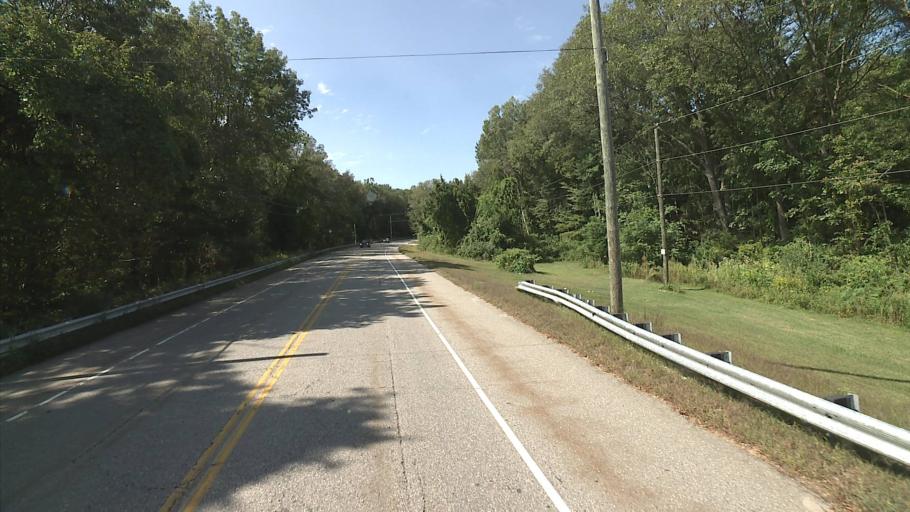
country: US
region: Connecticut
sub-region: New London County
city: Baltic
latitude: 41.5834
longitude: -72.1510
